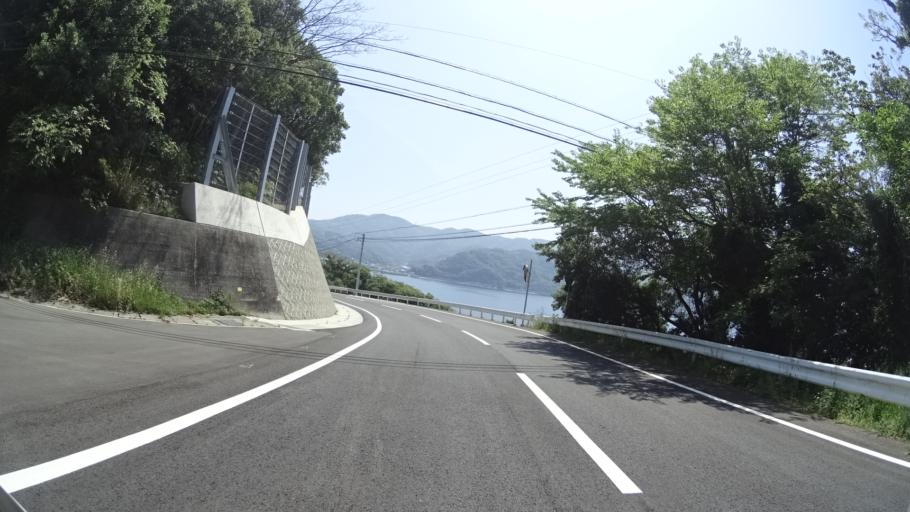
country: JP
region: Ehime
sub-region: Nishiuwa-gun
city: Ikata-cho
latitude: 33.3897
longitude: 132.1066
